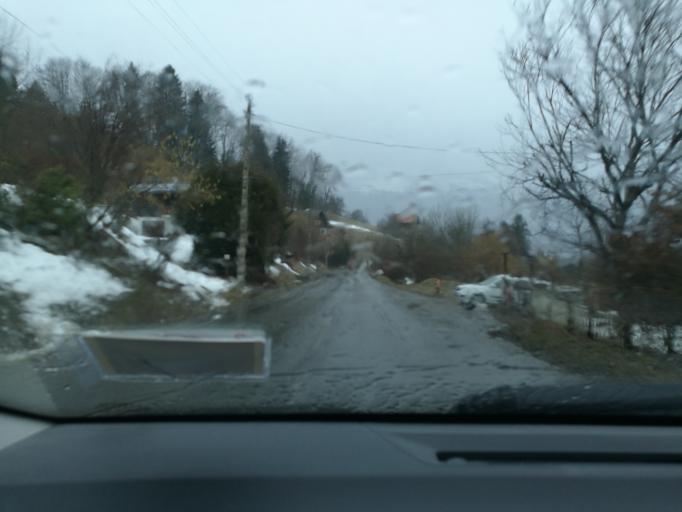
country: FR
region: Rhone-Alpes
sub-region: Departement de la Haute-Savoie
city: Saint-Gervais-les-Bains
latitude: 45.8792
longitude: 6.7045
